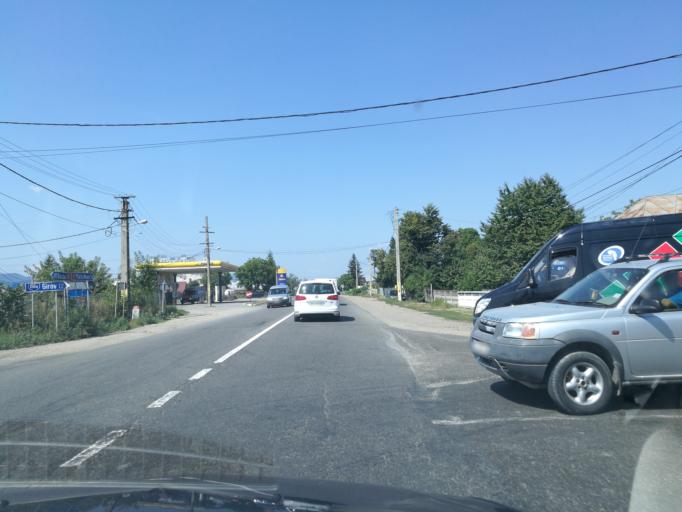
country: RO
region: Neamt
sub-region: Comuna Roznov
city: Chintinici
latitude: 46.8430
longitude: 26.4990
